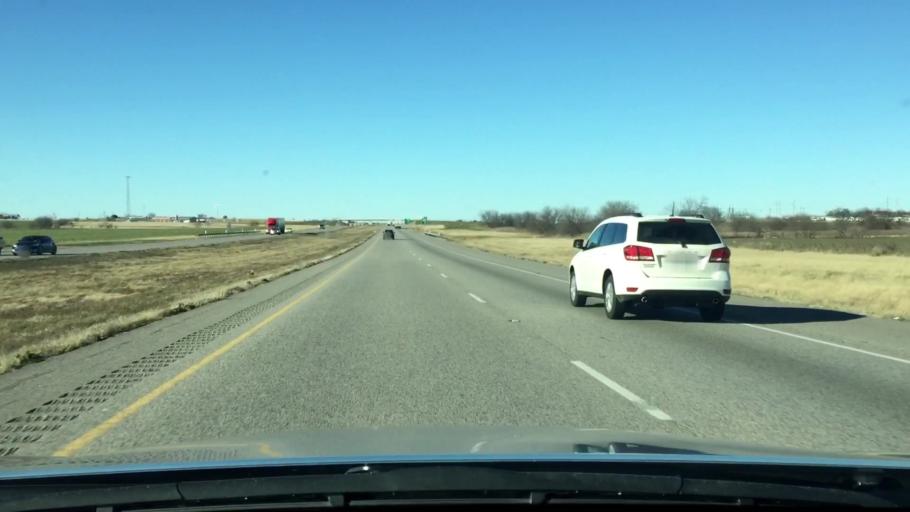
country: US
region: Texas
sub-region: Hill County
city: Itasca
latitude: 32.1450
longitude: -97.1235
